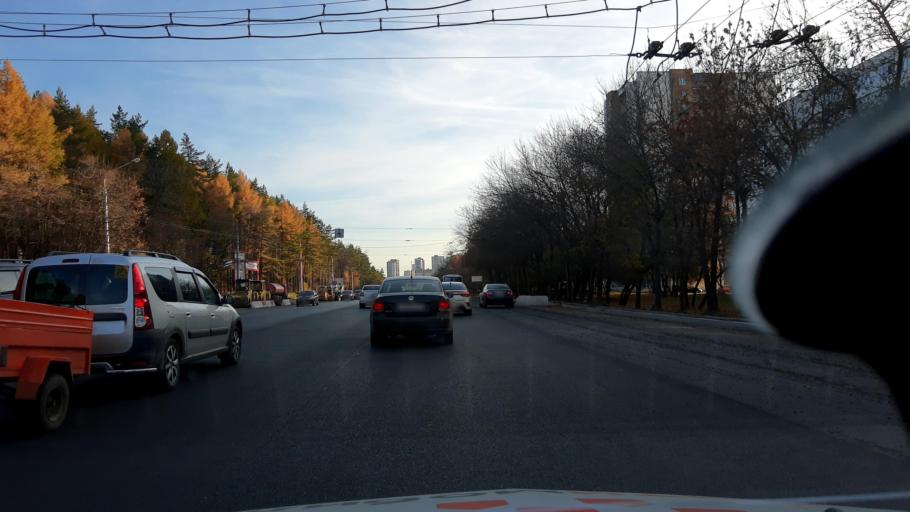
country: RU
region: Bashkortostan
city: Ufa
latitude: 54.7394
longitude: 56.0279
